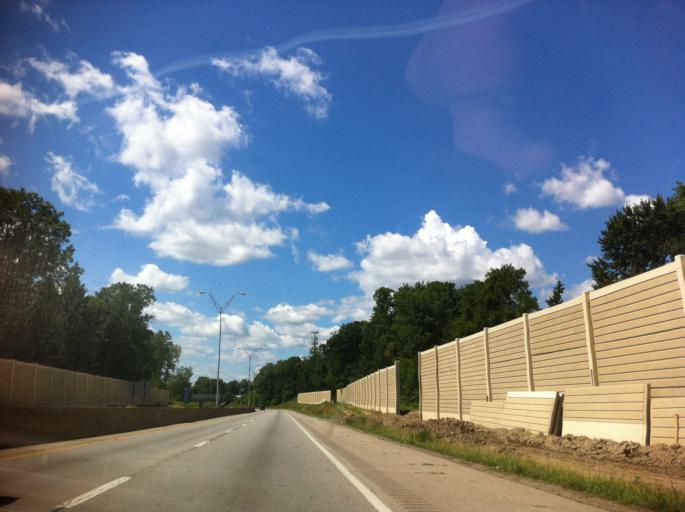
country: US
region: Ohio
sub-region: Lucas County
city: Ottawa Hills
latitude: 41.6887
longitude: -83.6574
